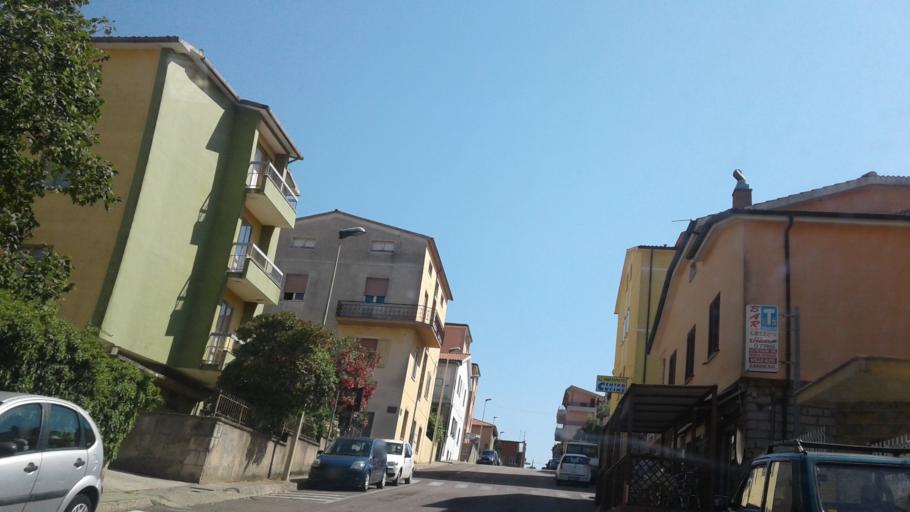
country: IT
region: Sardinia
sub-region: Provincia di Olbia-Tempio
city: Tempio Pausania
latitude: 40.8985
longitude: 9.1082
